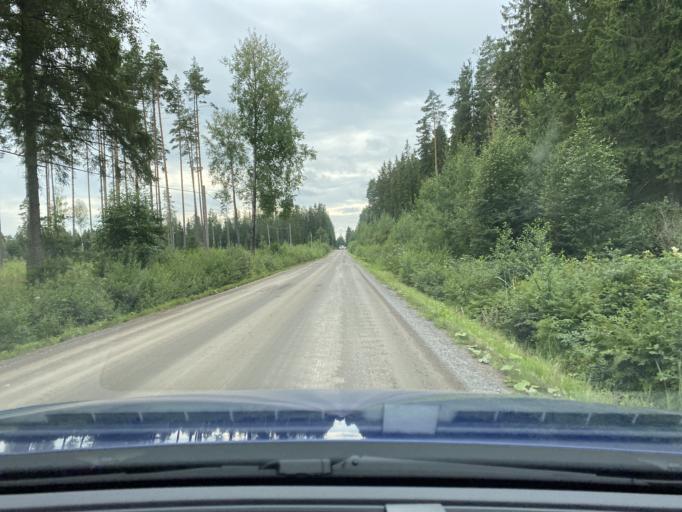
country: FI
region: Satakunta
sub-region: Rauma
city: Kiukainen
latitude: 61.1397
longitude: 21.9936
